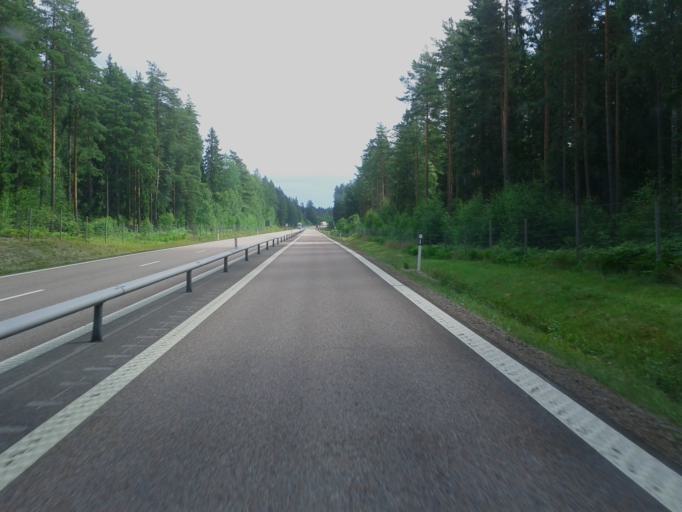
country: SE
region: Dalarna
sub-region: Saters Kommun
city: Saeter
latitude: 60.3259
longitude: 15.8649
